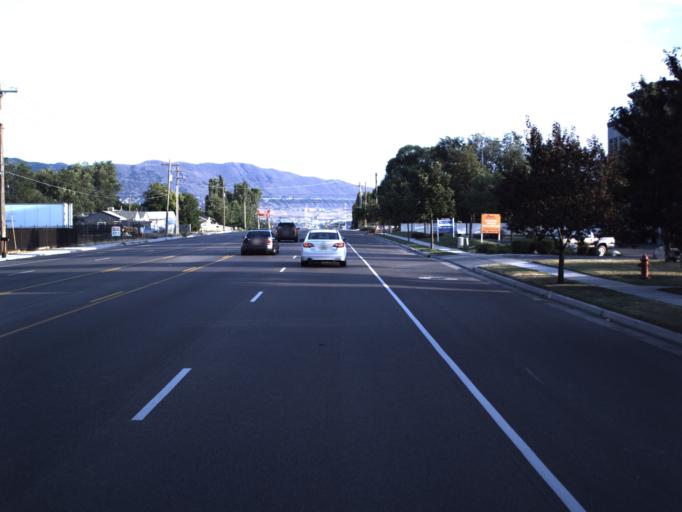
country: US
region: Utah
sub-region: Salt Lake County
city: Draper
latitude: 40.5406
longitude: -111.8915
